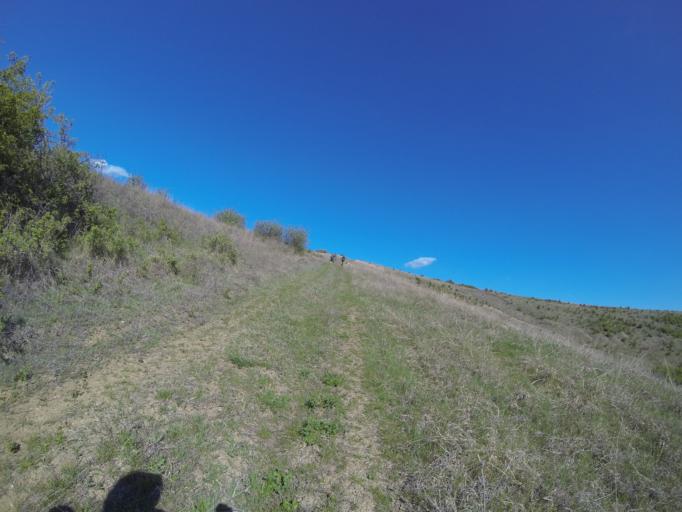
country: RO
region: Dolj
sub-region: Comuna Goesti
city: Goesti
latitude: 44.4935
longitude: 23.7664
